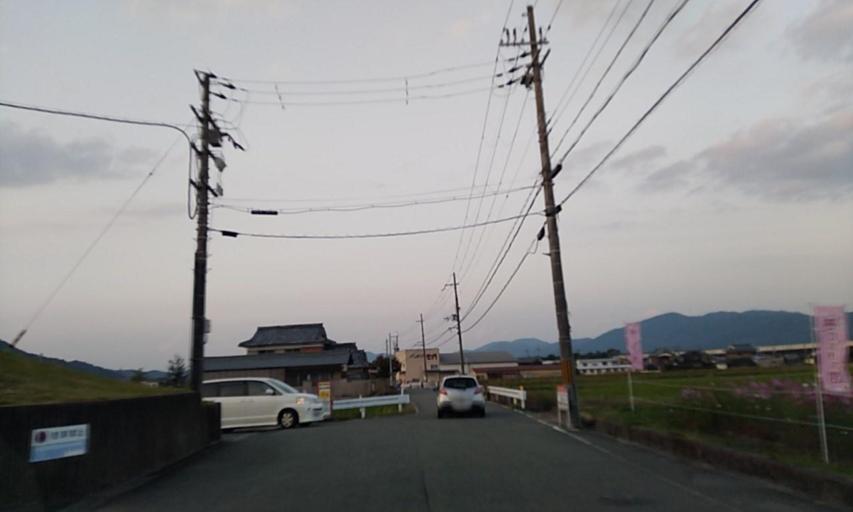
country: JP
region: Kyoto
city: Kameoka
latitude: 35.0149
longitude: 135.5517
